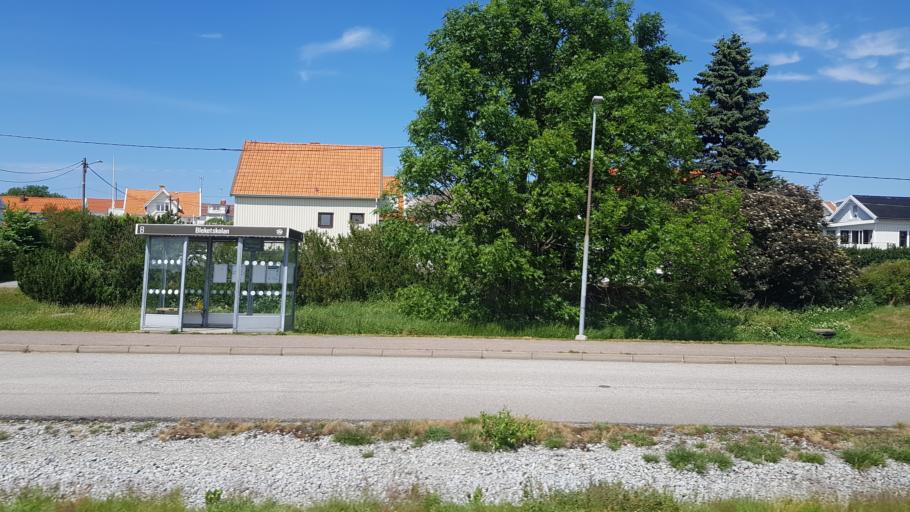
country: SE
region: Vaestra Goetaland
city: Ronnang
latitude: 57.9505
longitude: 11.5698
